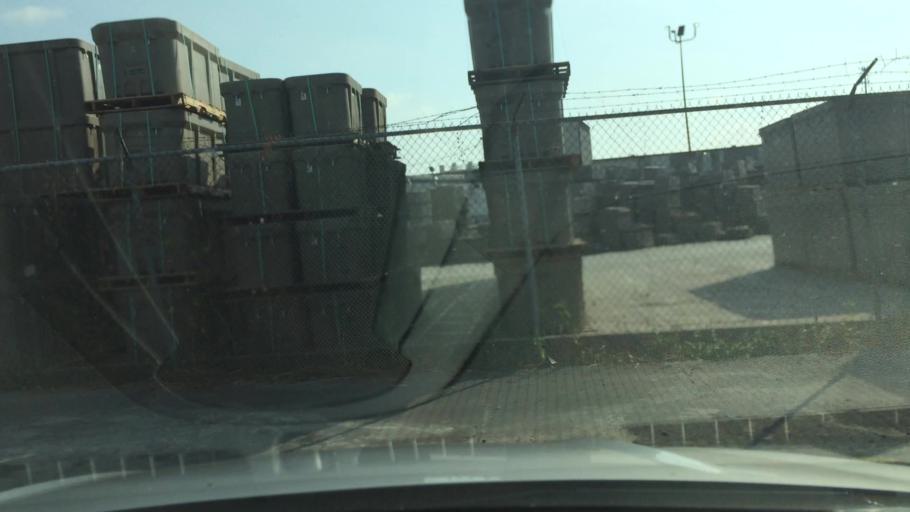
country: US
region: Tennessee
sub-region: Loudon County
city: Lenoir City
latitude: 35.7840
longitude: -84.2676
